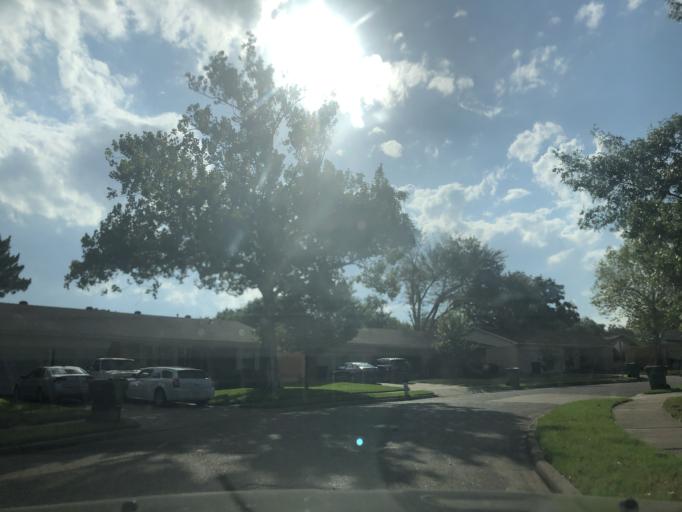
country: US
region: Texas
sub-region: Dallas County
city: Garland
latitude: 32.8901
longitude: -96.6576
